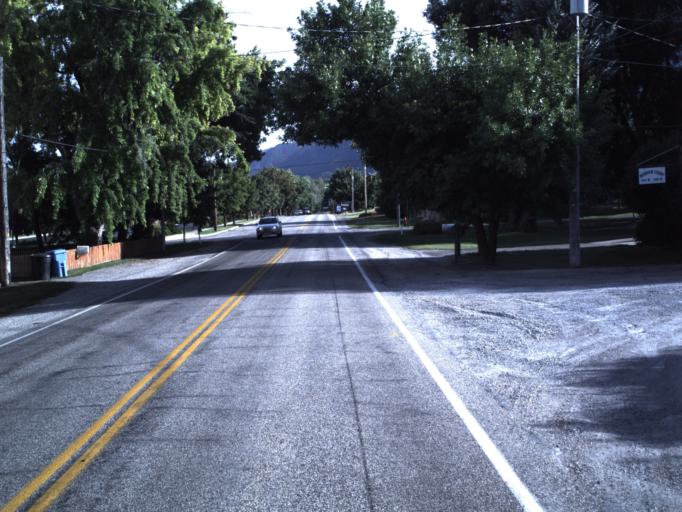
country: US
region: Utah
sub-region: Cache County
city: Mendon
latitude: 41.7107
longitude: -111.9792
